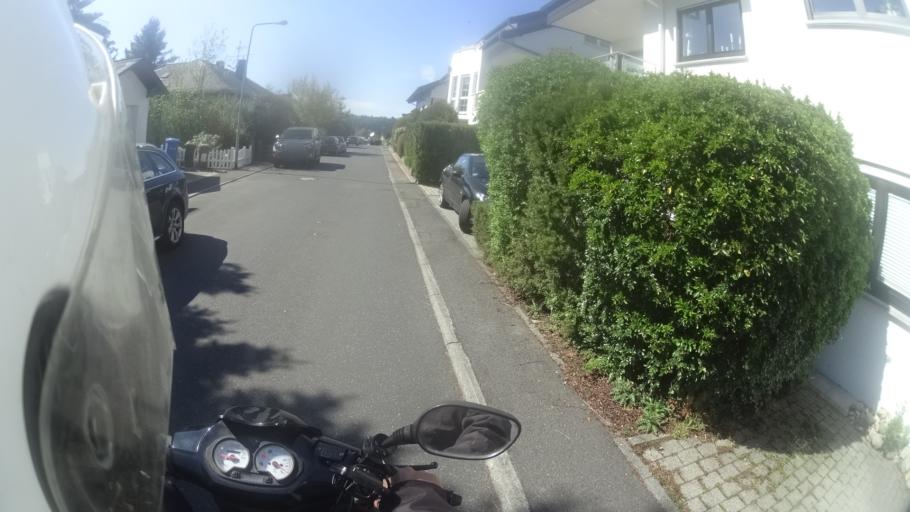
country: DE
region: Hesse
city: Taunusstein
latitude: 50.1314
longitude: 8.1363
